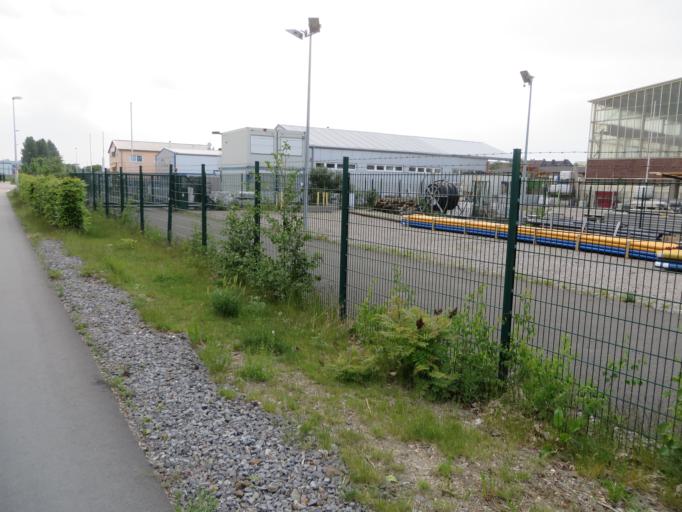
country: DE
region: North Rhine-Westphalia
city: Witten
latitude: 51.4429
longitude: 7.3510
